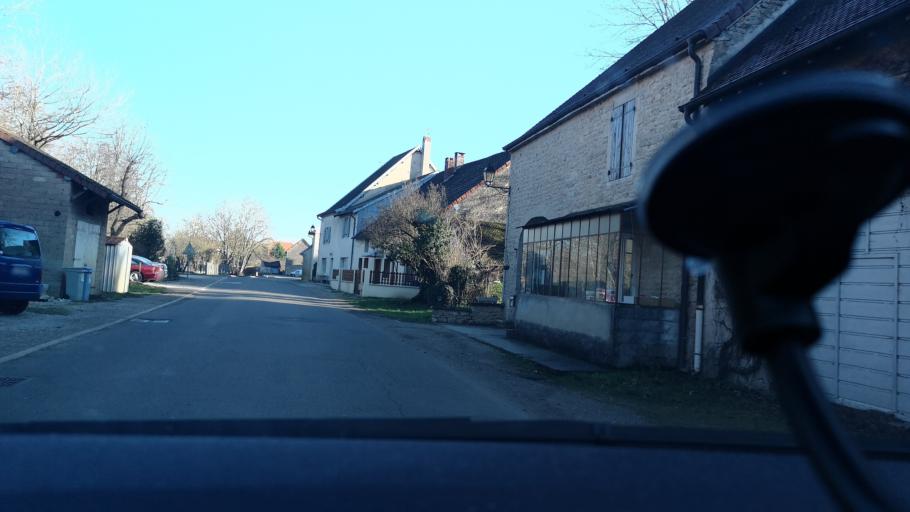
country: FR
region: Franche-Comte
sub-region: Departement du Jura
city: Bletterans
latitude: 46.7606
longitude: 5.5244
